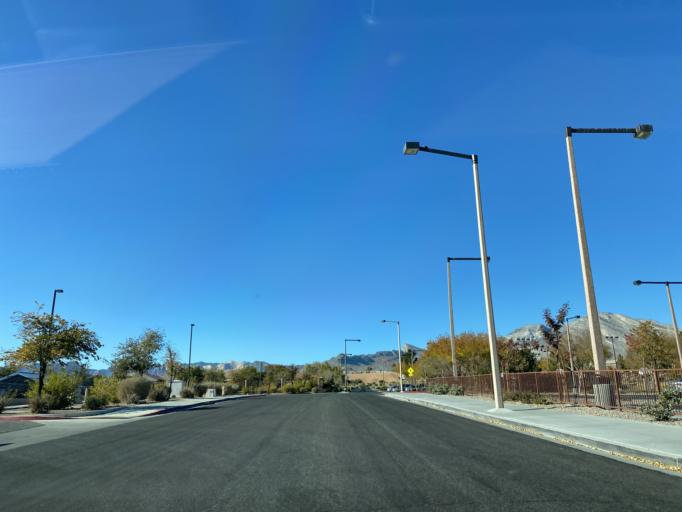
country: US
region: Nevada
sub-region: Clark County
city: Summerlin South
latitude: 36.1683
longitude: -115.3445
